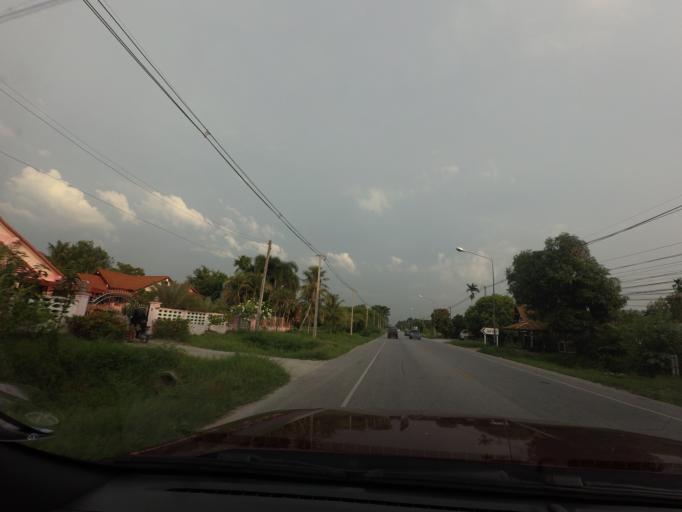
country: TH
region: Pattani
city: Mae Lan
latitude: 6.6322
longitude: 101.1868
